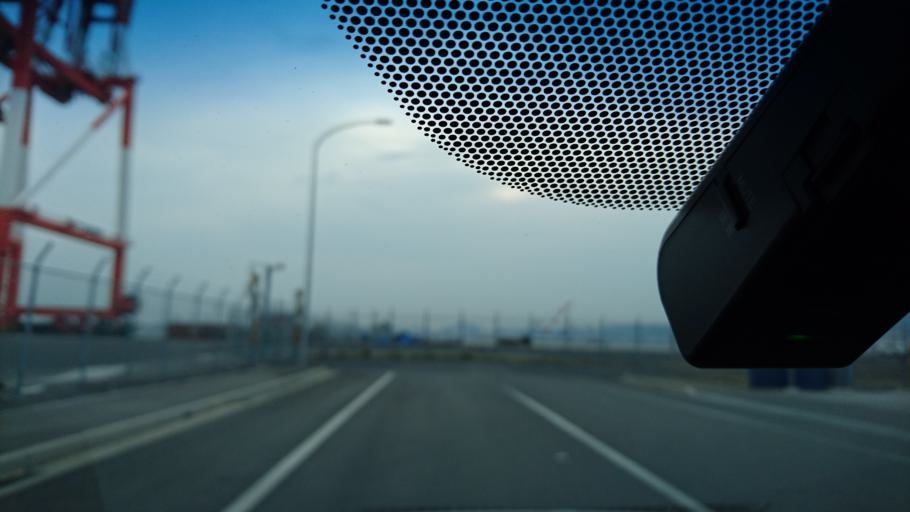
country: JP
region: Hyogo
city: Ashiya
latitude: 34.6845
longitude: 135.2546
